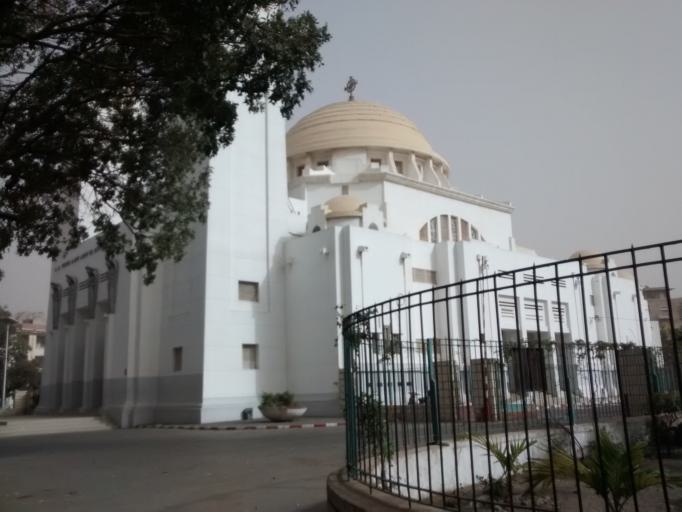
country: SN
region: Dakar
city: Dakar
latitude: 14.6658
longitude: -17.4379
